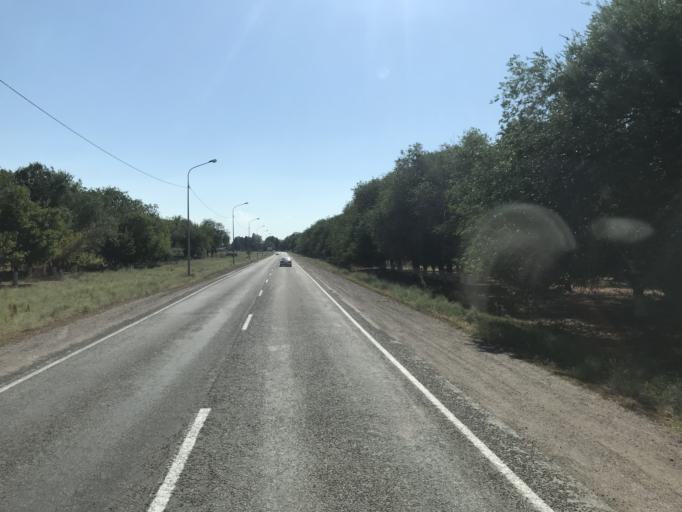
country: KZ
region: Zhambyl
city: Georgiyevka
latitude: 43.2388
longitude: 74.7676
